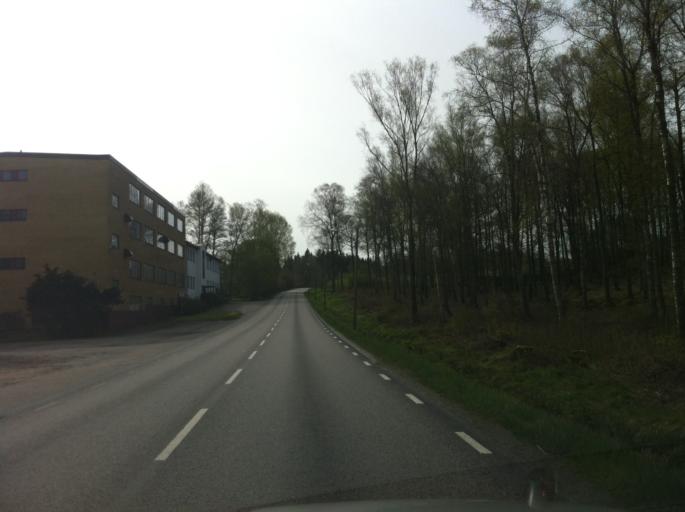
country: SE
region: Vaestra Goetaland
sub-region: Marks Kommun
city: Kinna
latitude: 57.4633
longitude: 12.7184
